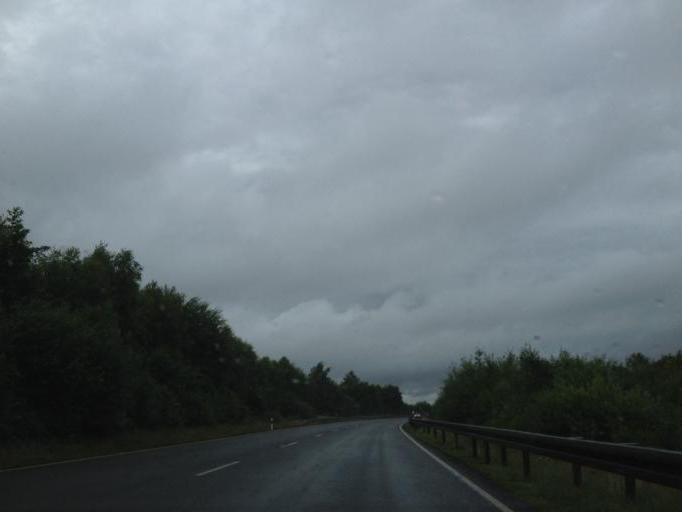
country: DE
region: Bavaria
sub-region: Upper Franconia
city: Hohenberg an der Eger
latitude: 50.0817
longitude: 12.2032
